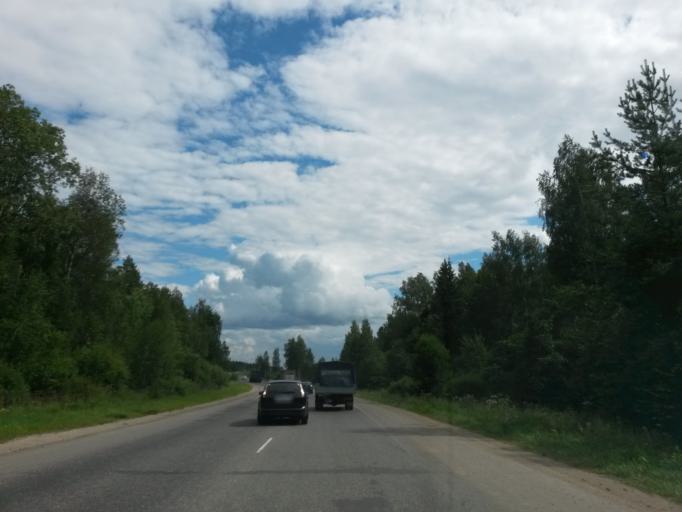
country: RU
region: Ivanovo
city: Novo-Talitsy
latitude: 57.0166
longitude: 40.7846
